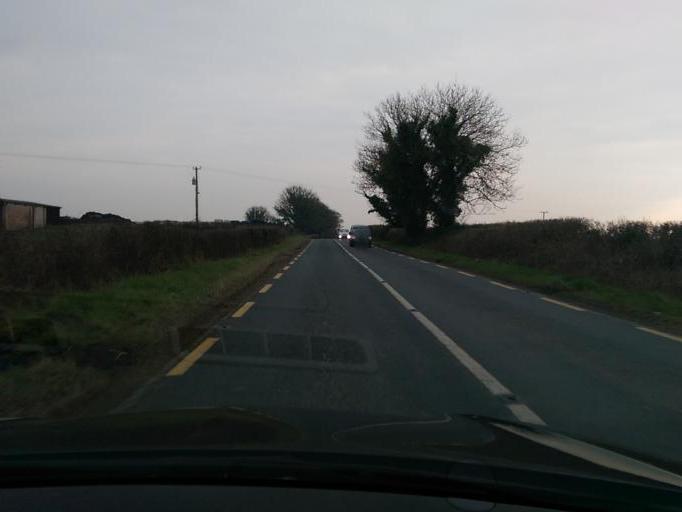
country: IE
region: Leinster
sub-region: An Longfort
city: Ballymahon
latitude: 53.5191
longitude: -7.8191
